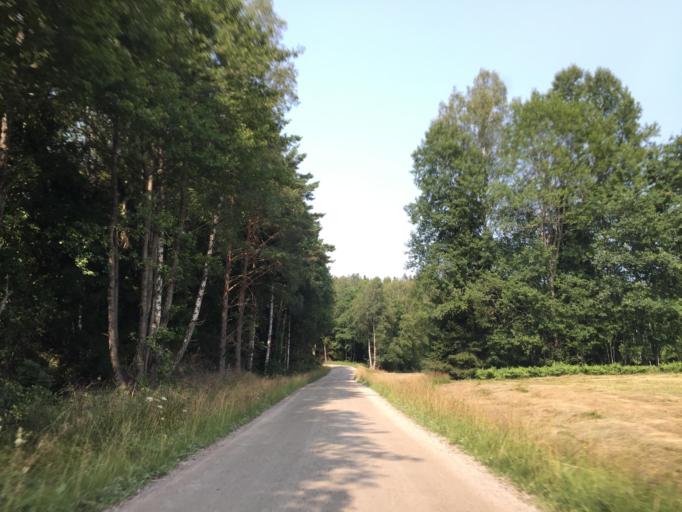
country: SE
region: Vaestra Goetaland
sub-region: Trollhattan
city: Sjuntorp
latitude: 58.2670
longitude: 12.1037
